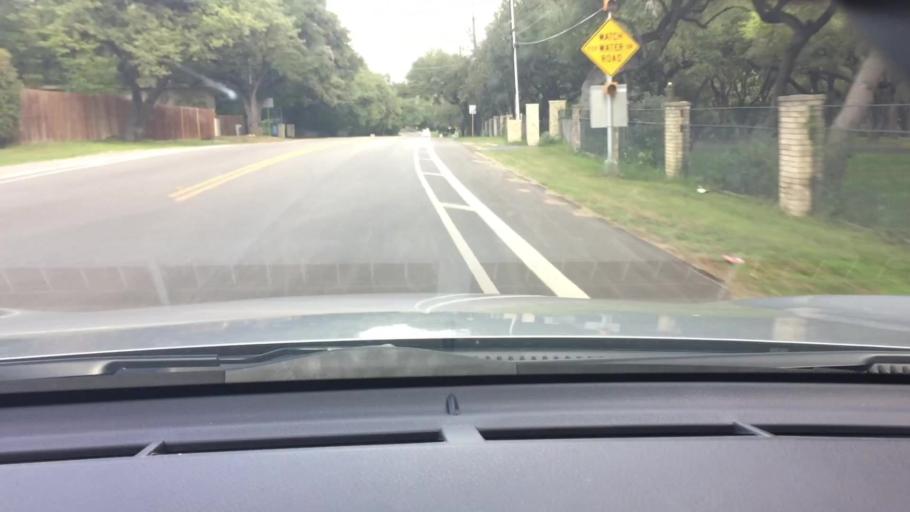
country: US
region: Texas
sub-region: Bexar County
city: Shavano Park
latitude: 29.5611
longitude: -98.5432
